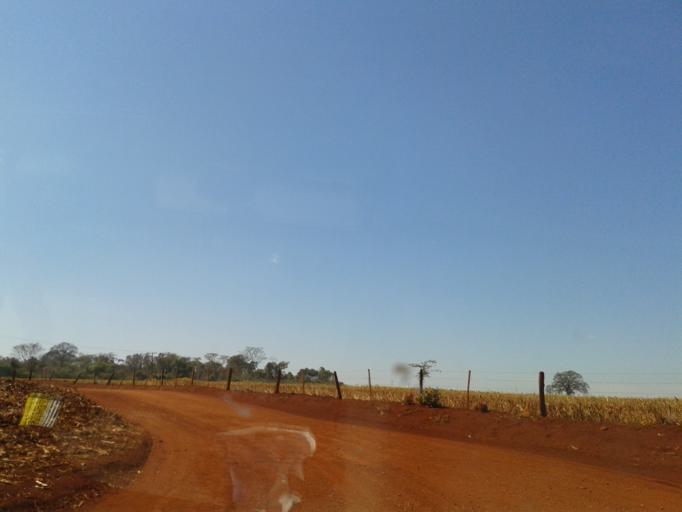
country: BR
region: Minas Gerais
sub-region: Capinopolis
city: Capinopolis
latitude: -18.6191
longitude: -49.4942
